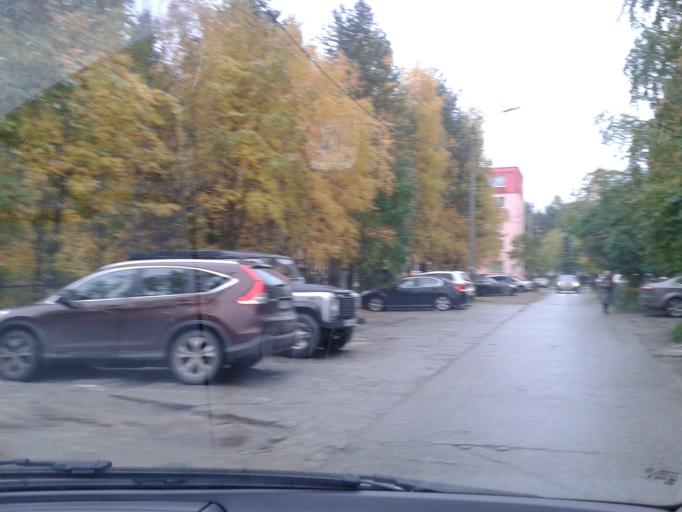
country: RU
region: Murmansk
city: Polyarnyye Zori
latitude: 67.3673
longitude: 32.4999
